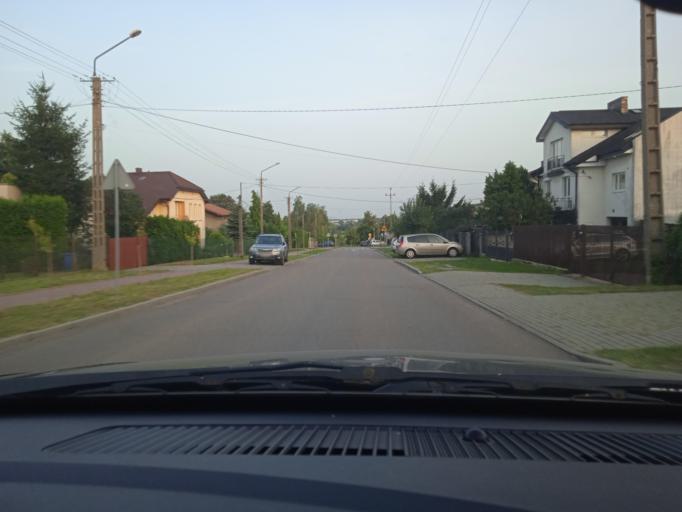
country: PL
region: Masovian Voivodeship
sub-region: Powiat nowodworski
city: Nowy Dwor Mazowiecki
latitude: 52.4451
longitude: 20.7005
